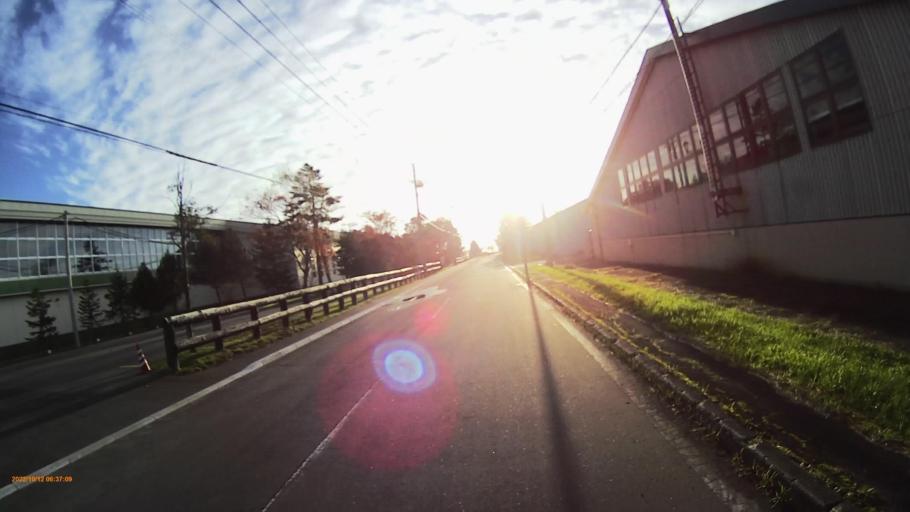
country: JP
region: Hokkaido
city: Kushiro
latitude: 42.8923
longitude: 143.9371
